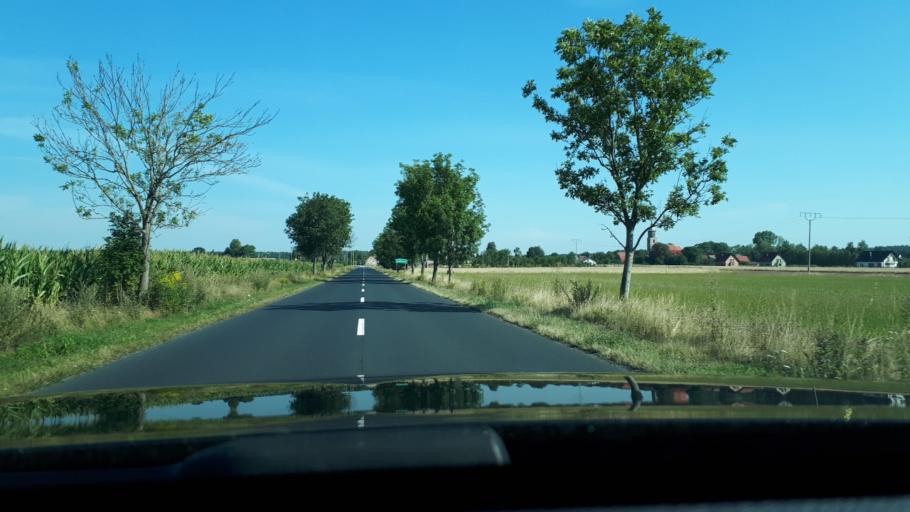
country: PL
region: Lower Silesian Voivodeship
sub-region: Powiat lubanski
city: Pisarzowice
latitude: 51.2032
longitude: 15.2476
